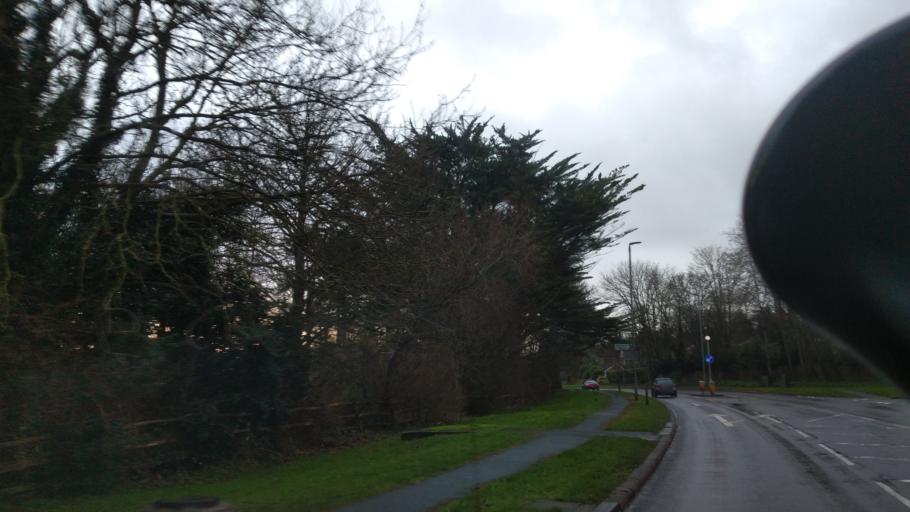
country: GB
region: England
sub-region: East Sussex
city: Eastbourne
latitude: 50.7931
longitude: 0.2563
